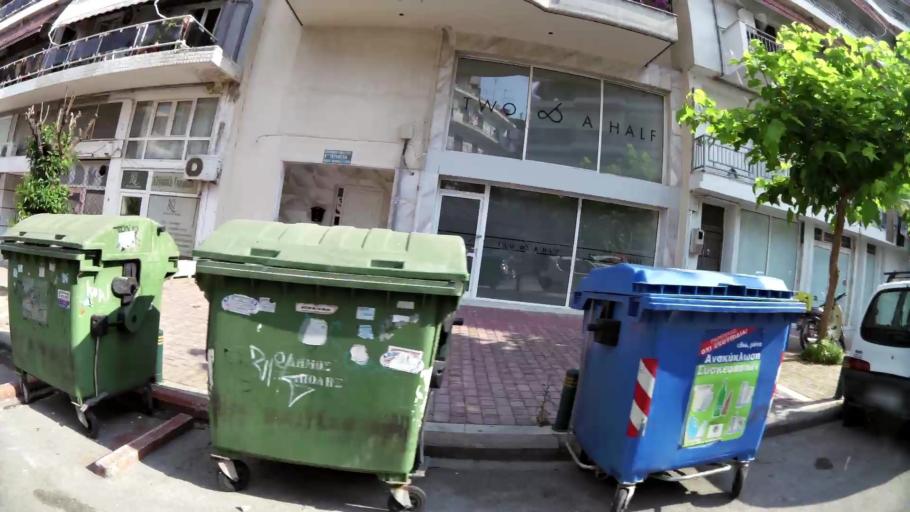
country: GR
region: Central Macedonia
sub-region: Nomos Thessalonikis
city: Stavroupoli
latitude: 40.6565
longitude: 22.9393
